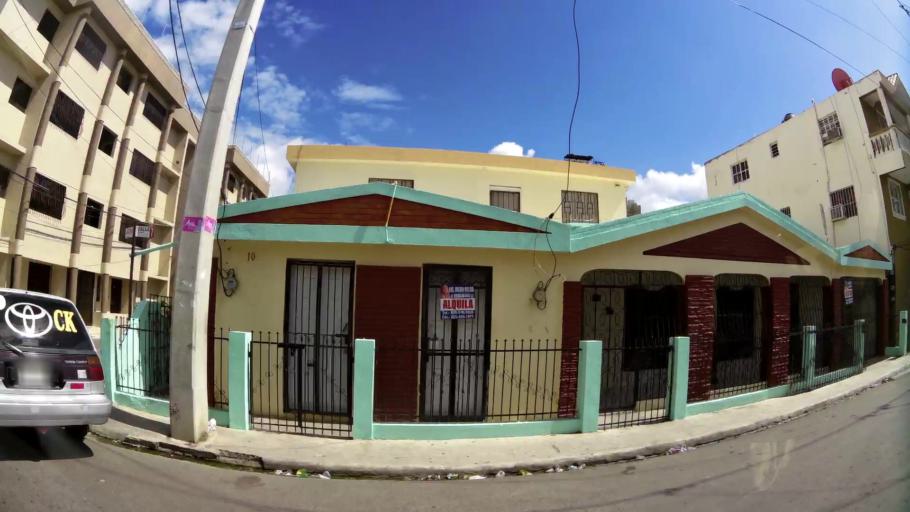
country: DO
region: Santiago
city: Santiago de los Caballeros
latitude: 19.4716
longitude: -70.6983
